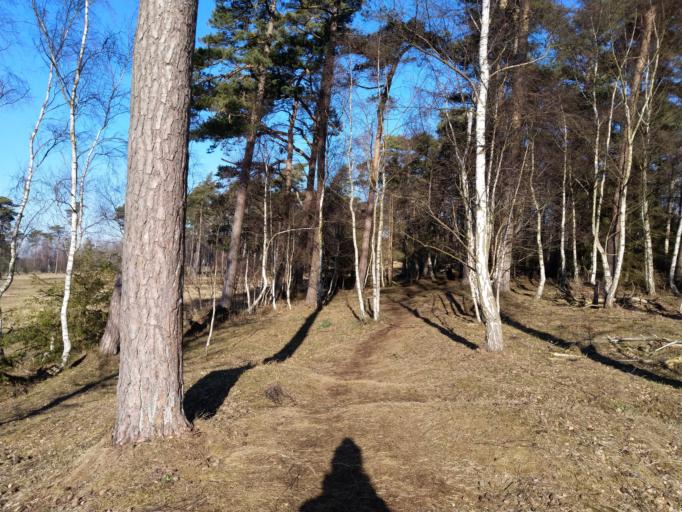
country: DK
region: Zealand
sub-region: Guldborgsund Kommune
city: Nykobing Falster
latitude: 54.6417
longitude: 11.9574
